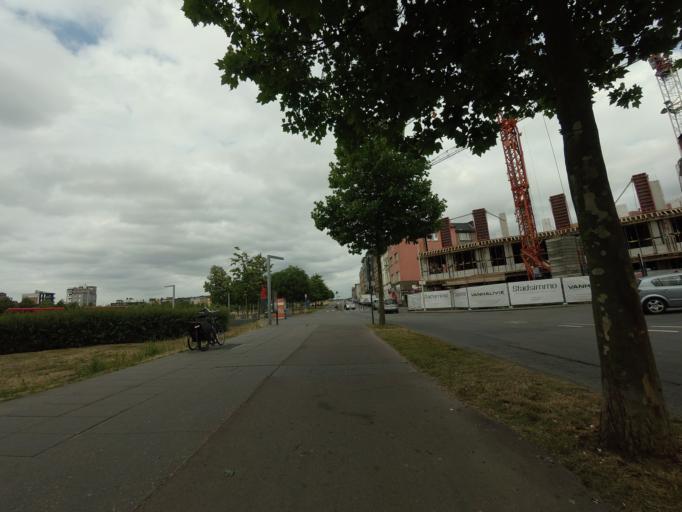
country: BE
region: Flanders
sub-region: Provincie Antwerpen
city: Antwerpen
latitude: 51.2299
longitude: 4.4204
